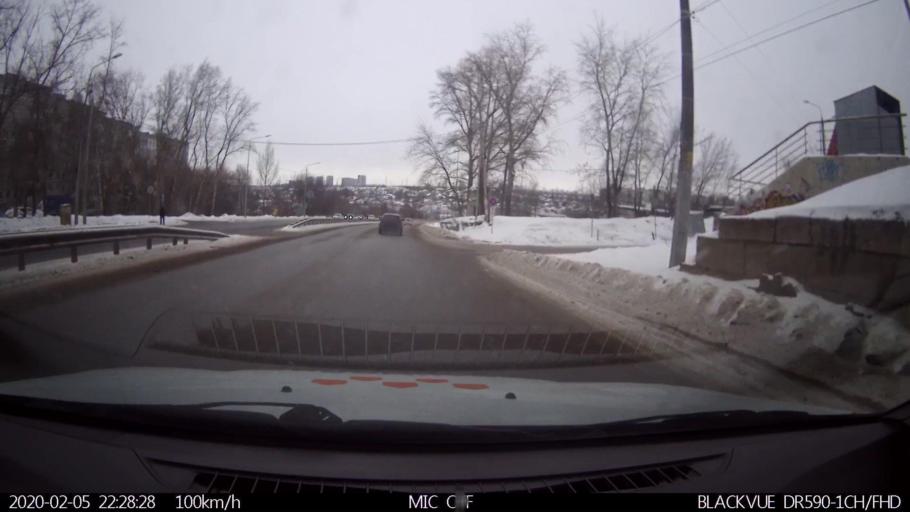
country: RU
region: Nizjnij Novgorod
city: Imeni Stepana Razina
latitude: 54.7573
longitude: 44.1339
